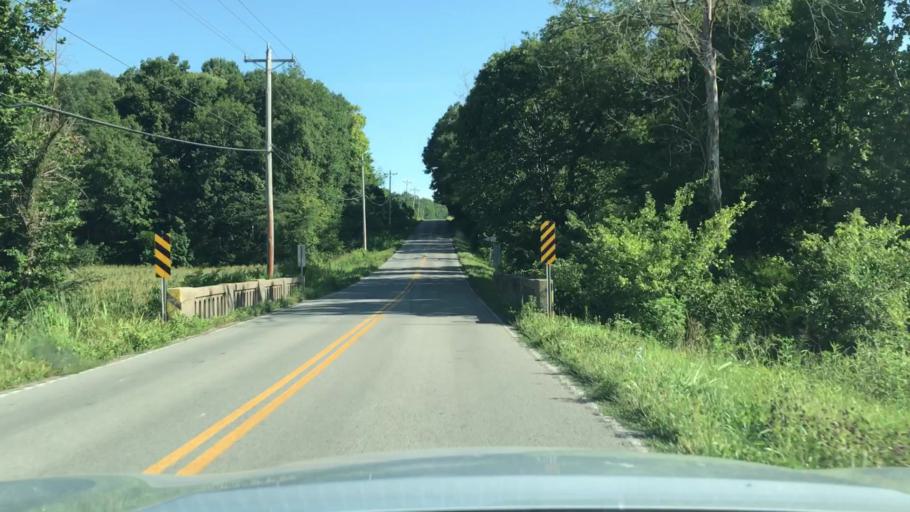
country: US
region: Kentucky
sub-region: Muhlenberg County
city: Greenville
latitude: 37.1023
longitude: -87.1266
